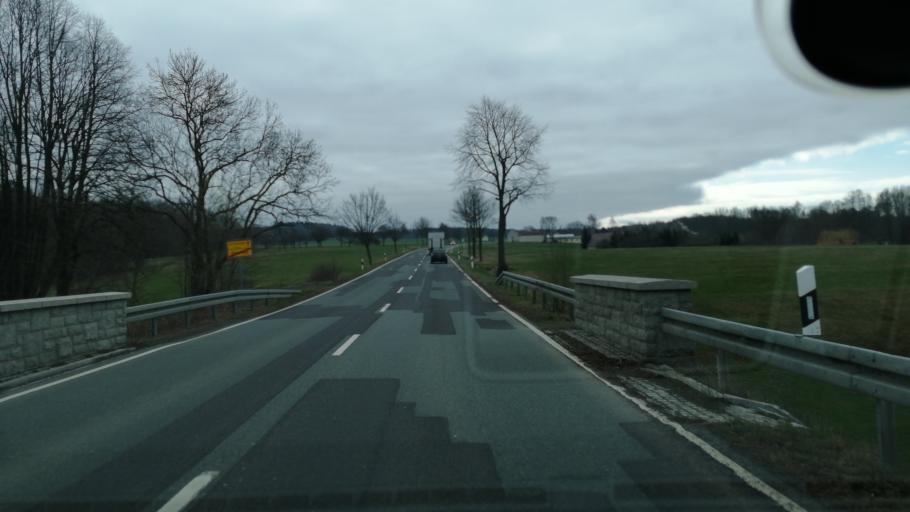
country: DE
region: Saxony
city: Niedercunnersdorf
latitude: 51.0629
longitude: 14.6916
